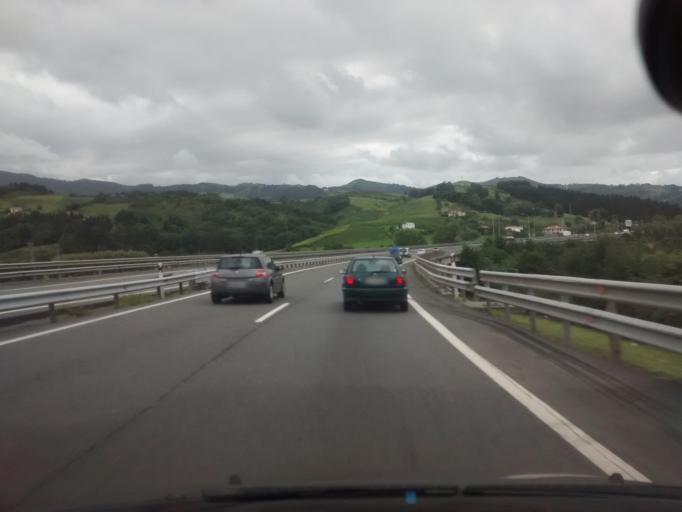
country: ES
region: Basque Country
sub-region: Provincia de Guipuzcoa
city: Orio
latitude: 43.2801
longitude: -2.1476
